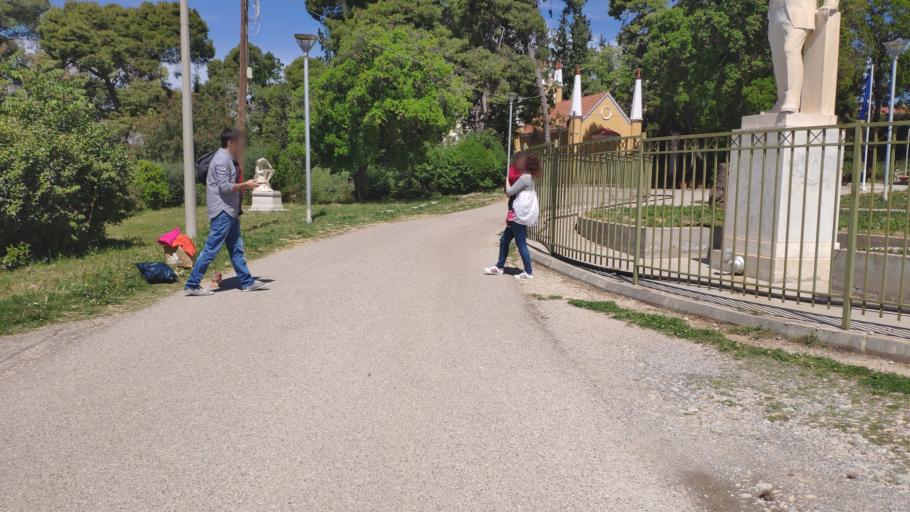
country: GR
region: Attica
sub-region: Nomarchia Athinas
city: Kifisia
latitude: 38.0647
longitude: 23.8122
